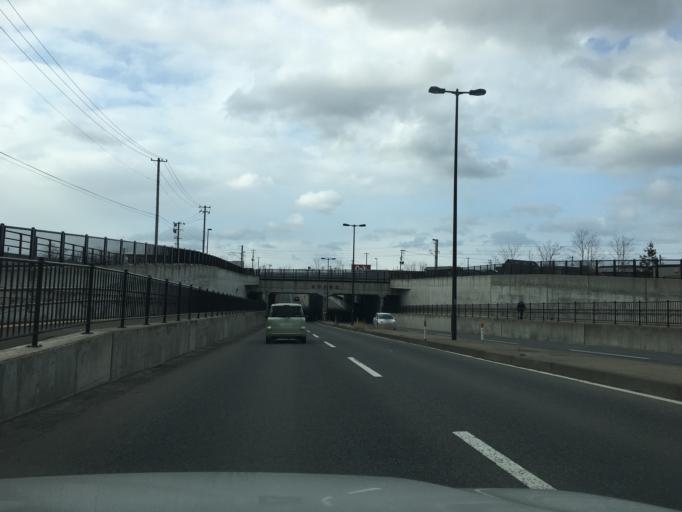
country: JP
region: Aomori
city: Aomori Shi
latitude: 40.8256
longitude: 140.7052
